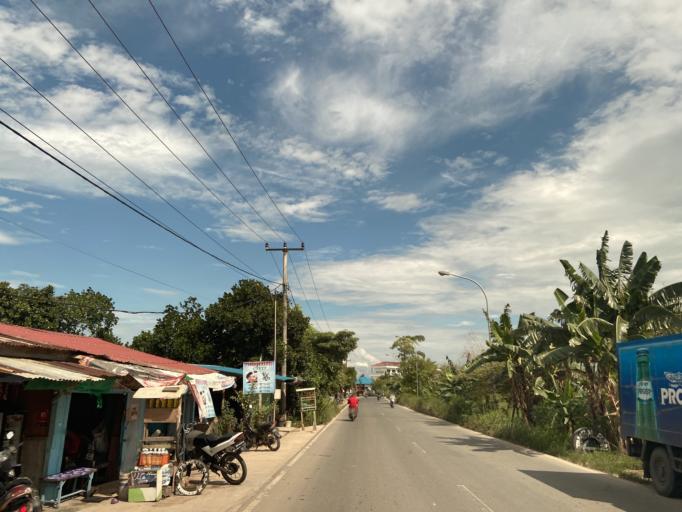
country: SG
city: Singapore
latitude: 1.0366
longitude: 103.9379
